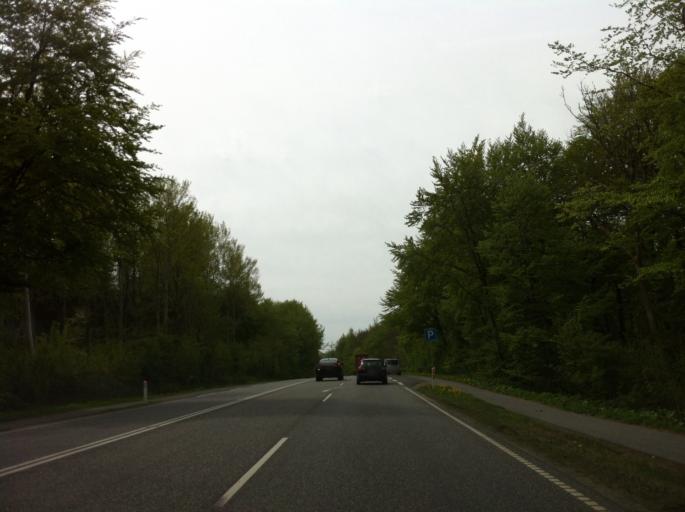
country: DK
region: Zealand
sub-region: Lejre Kommune
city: Osted
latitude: 55.5146
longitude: 11.8957
